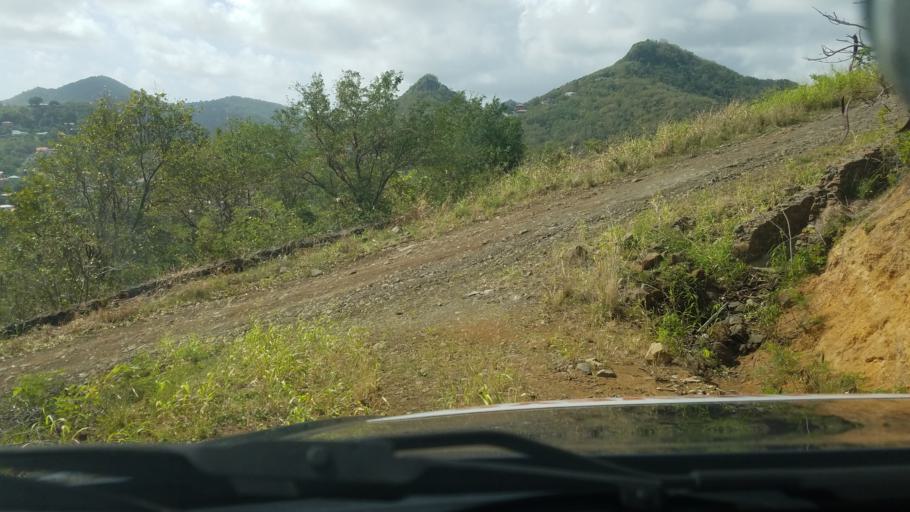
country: LC
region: Gros-Islet
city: Gros Islet
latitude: 14.0642
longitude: -60.9474
